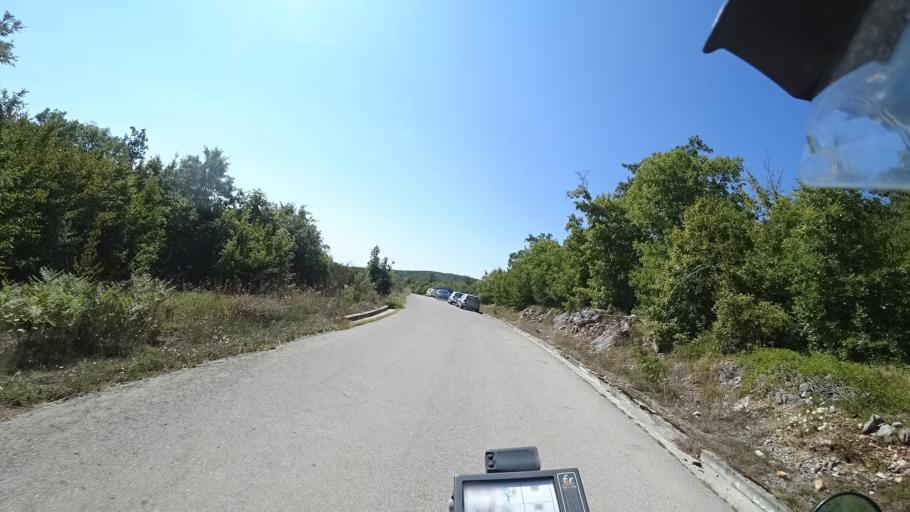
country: HR
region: Licko-Senjska
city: Otocac
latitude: 44.7435
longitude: 15.3793
